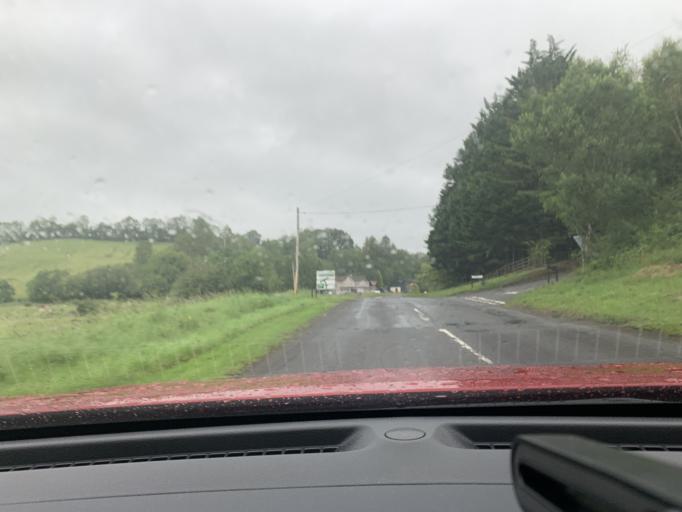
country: GB
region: Northern Ireland
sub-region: Fermanagh District
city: Enniskillen
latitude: 54.3187
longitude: -7.6833
